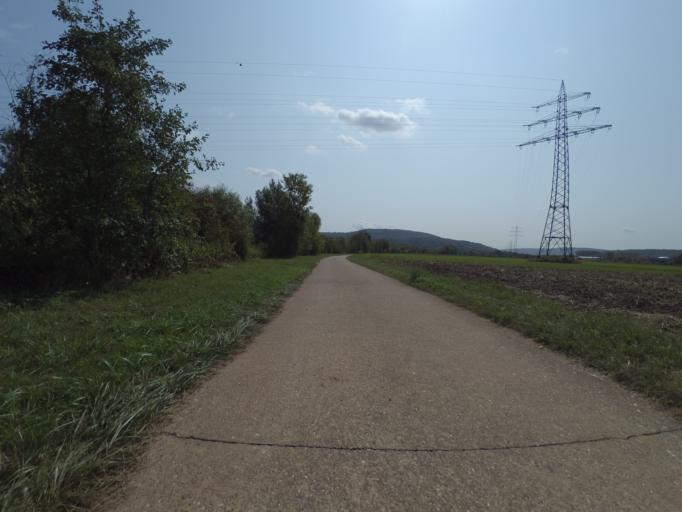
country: DE
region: Saarland
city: Merzig
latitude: 49.4527
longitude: 6.6280
